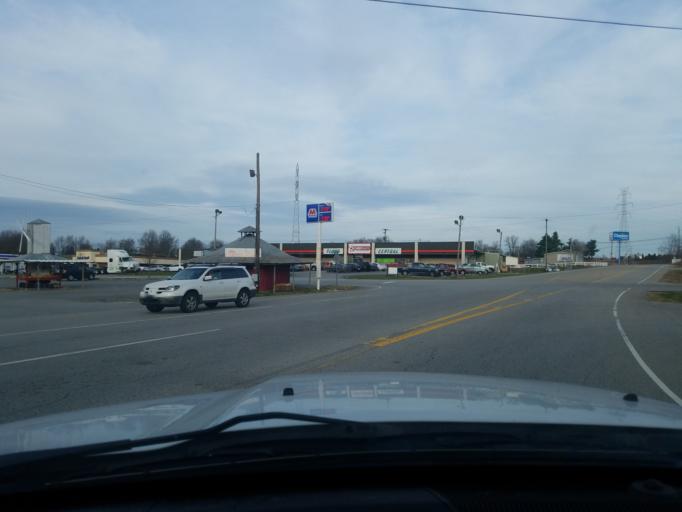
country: US
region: Indiana
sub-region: Floyd County
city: Georgetown
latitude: 38.2889
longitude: -85.9133
